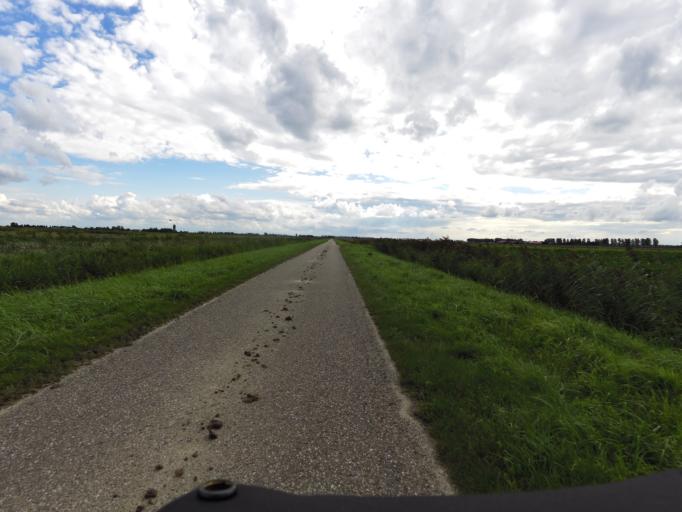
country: NL
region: South Holland
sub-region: Gemeente Goeree-Overflakkee
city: Middelharnis
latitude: 51.7153
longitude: 4.2428
